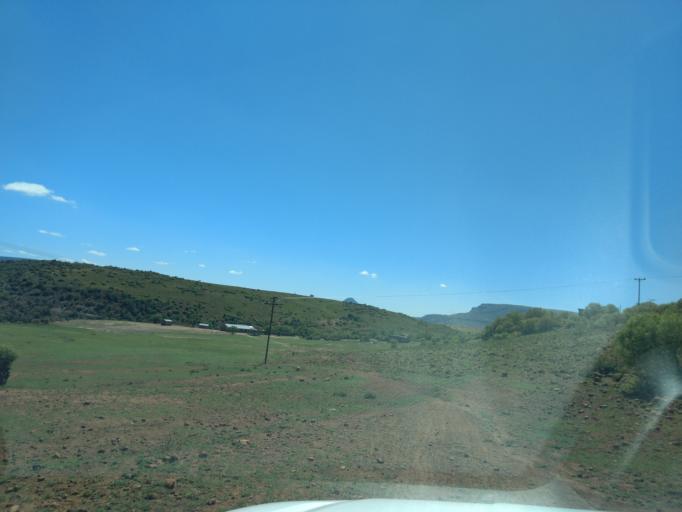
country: LS
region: Maseru
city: Maseru
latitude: -29.4496
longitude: 27.3811
